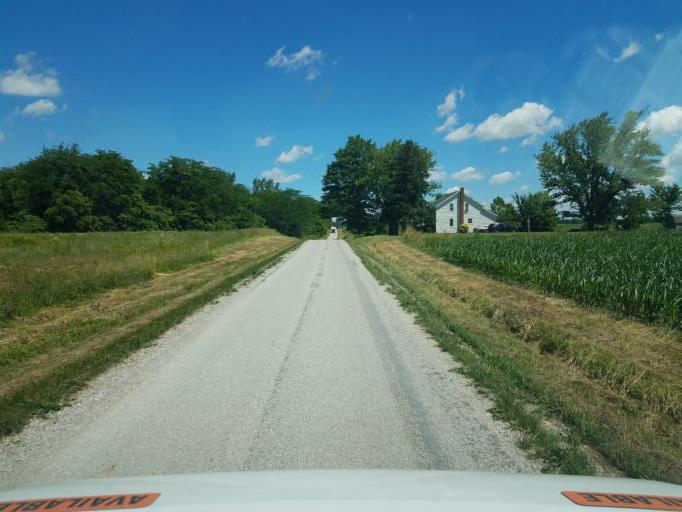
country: US
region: Ohio
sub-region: Crawford County
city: Bucyrus
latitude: 40.6933
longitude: -82.9390
